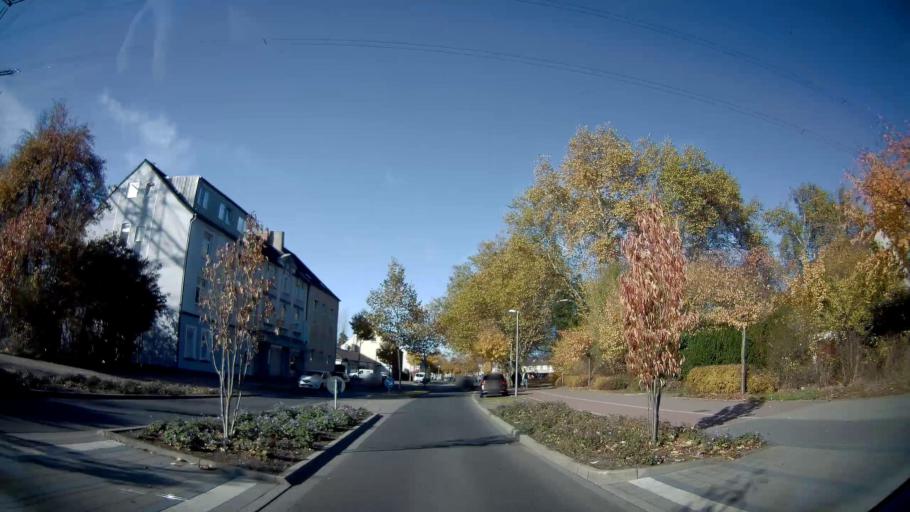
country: DE
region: North Rhine-Westphalia
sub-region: Regierungsbezirk Munster
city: Gladbeck
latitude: 51.5483
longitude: 7.0111
